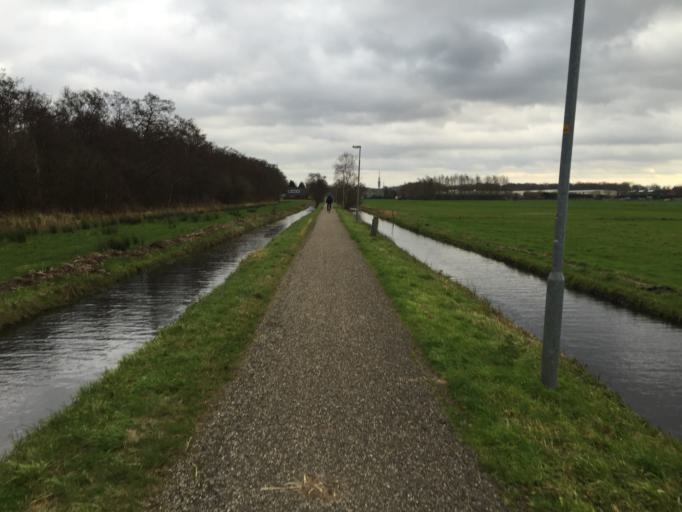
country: NL
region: North Holland
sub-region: Gemeente Wijdemeren
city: Kortenhoef
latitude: 52.2632
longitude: 5.1121
